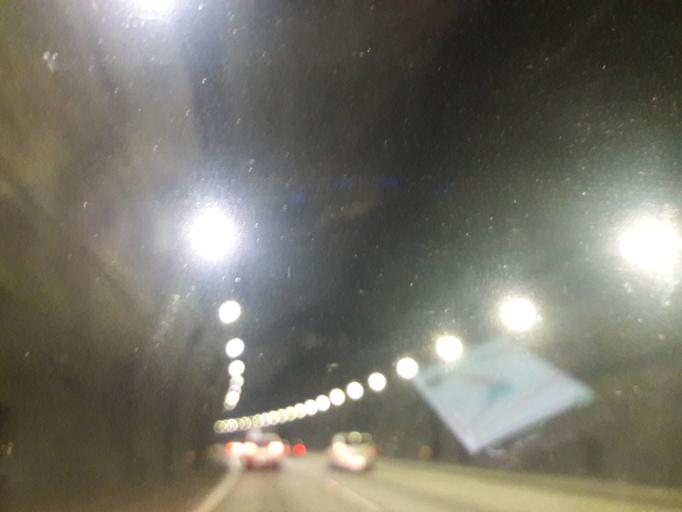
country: BR
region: Sao Paulo
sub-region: Cubatao
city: Cubatao
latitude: -23.8869
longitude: -46.5012
